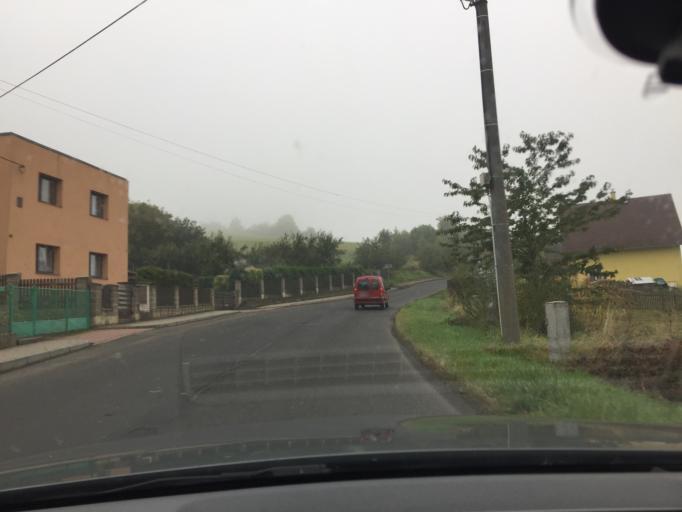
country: CZ
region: Ustecky
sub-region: Okres Usti nad Labem
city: Usti nad Labem
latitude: 50.6869
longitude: 14.0440
